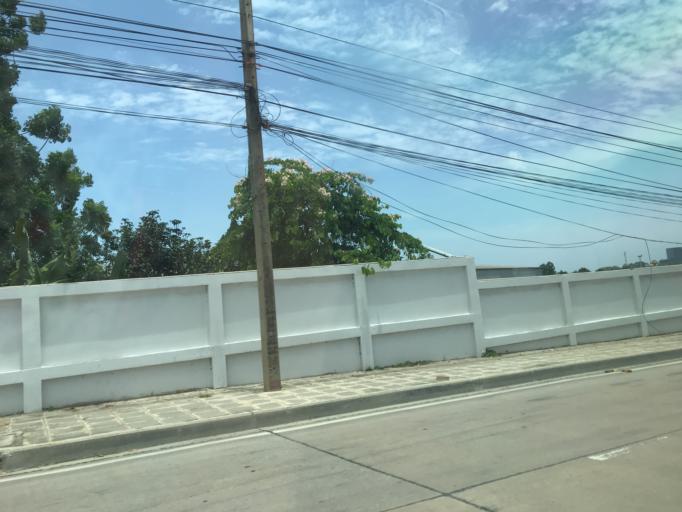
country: TH
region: Chon Buri
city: Si Racha
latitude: 13.1109
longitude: 100.9504
